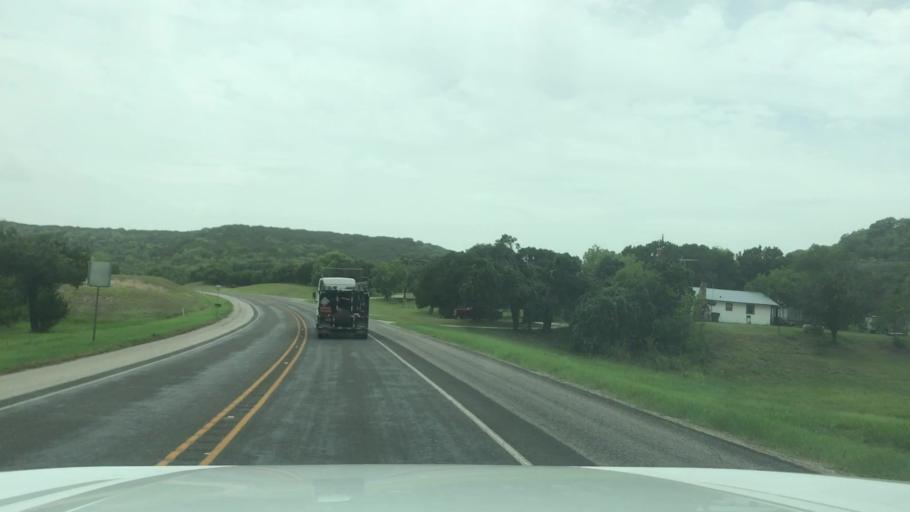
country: US
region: Texas
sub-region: Bosque County
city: Meridian
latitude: 31.9061
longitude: -97.6610
